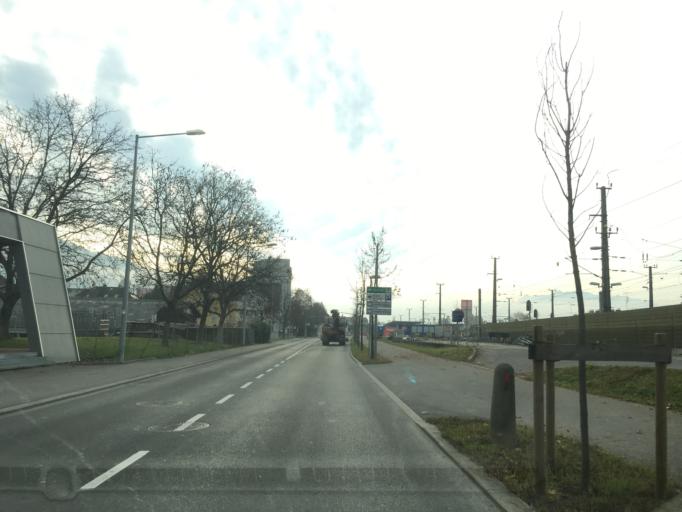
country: AT
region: Vorarlberg
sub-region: Politischer Bezirk Dornbirn
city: Hohenems
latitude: 47.3666
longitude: 9.6838
